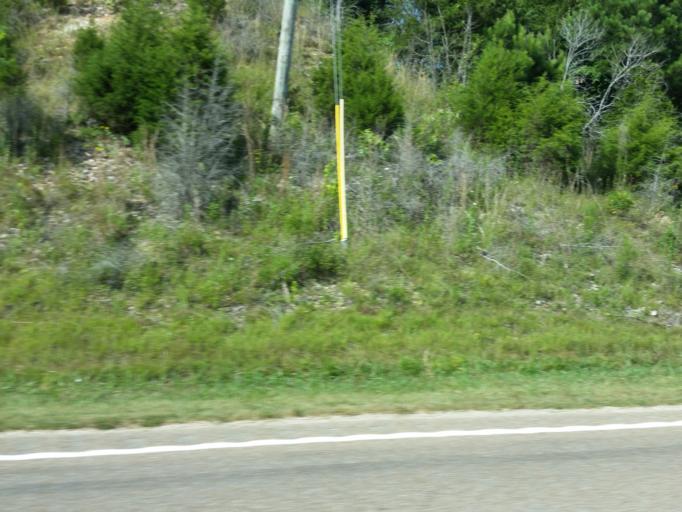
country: US
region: Tennessee
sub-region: Decatur County
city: Parsons
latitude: 35.6366
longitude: -88.0751
